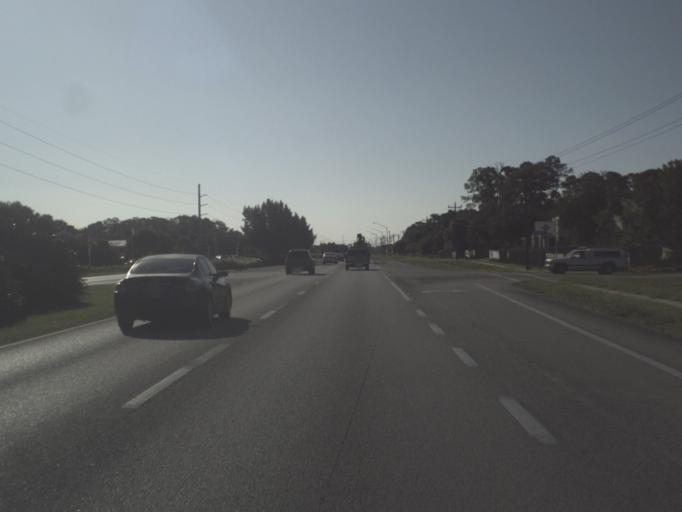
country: US
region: Florida
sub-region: Lee County
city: Palmona Park
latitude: 26.6732
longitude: -81.8955
